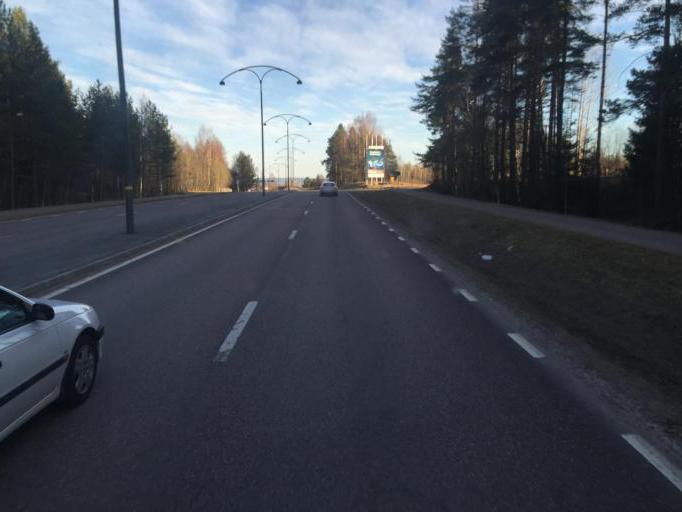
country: SE
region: Dalarna
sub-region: Borlange Kommun
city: Borlaenge
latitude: 60.5034
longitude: 15.3898
